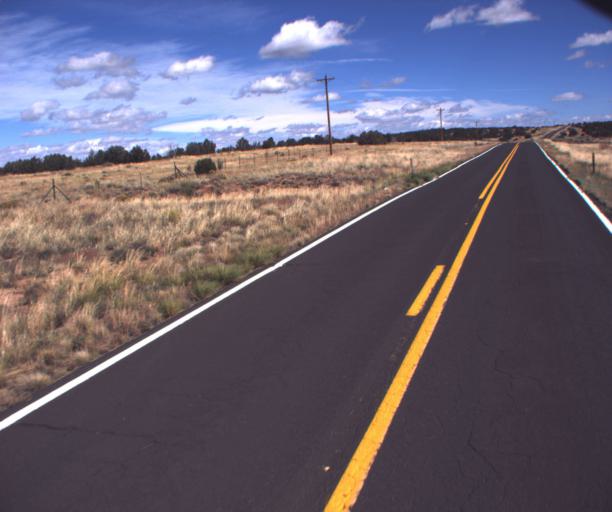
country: US
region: New Mexico
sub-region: McKinley County
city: Zuni Pueblo
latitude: 34.9813
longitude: -109.1273
